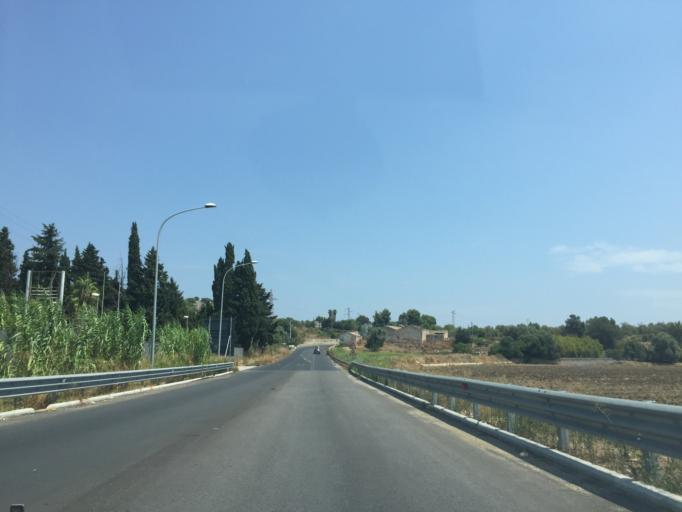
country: IT
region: Sicily
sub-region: Provincia di Siracusa
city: Siracusa
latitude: 37.0752
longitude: 15.2497
